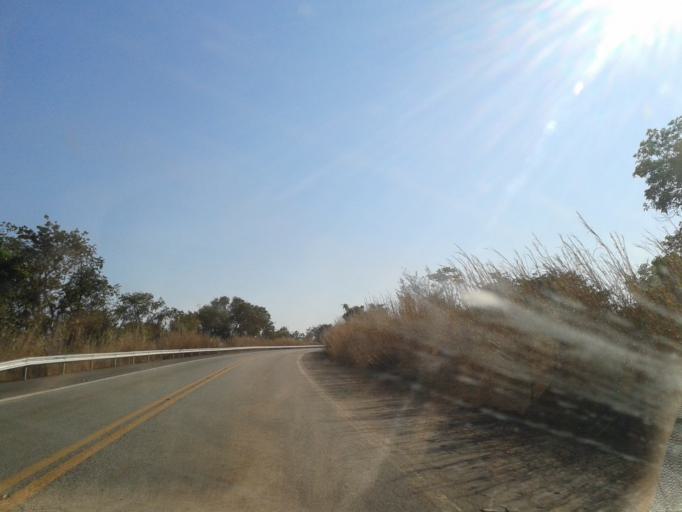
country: BR
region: Goias
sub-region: Mozarlandia
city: Mozarlandia
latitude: -14.9422
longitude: -50.5779
